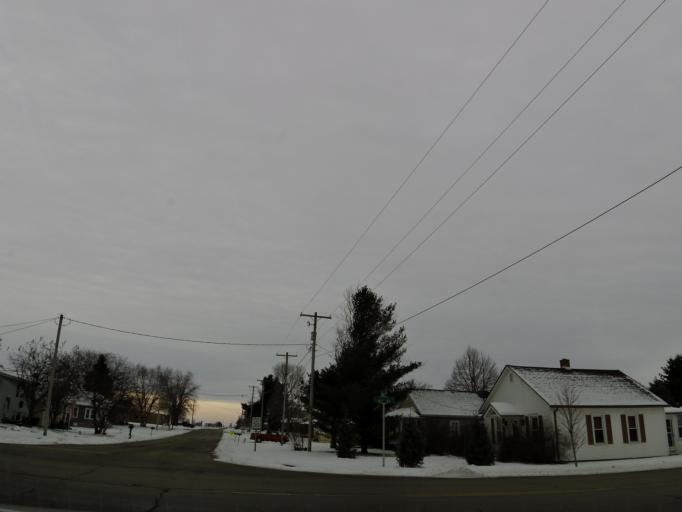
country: US
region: Illinois
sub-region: LaSalle County
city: Peru
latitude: 41.2623
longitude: -89.1259
